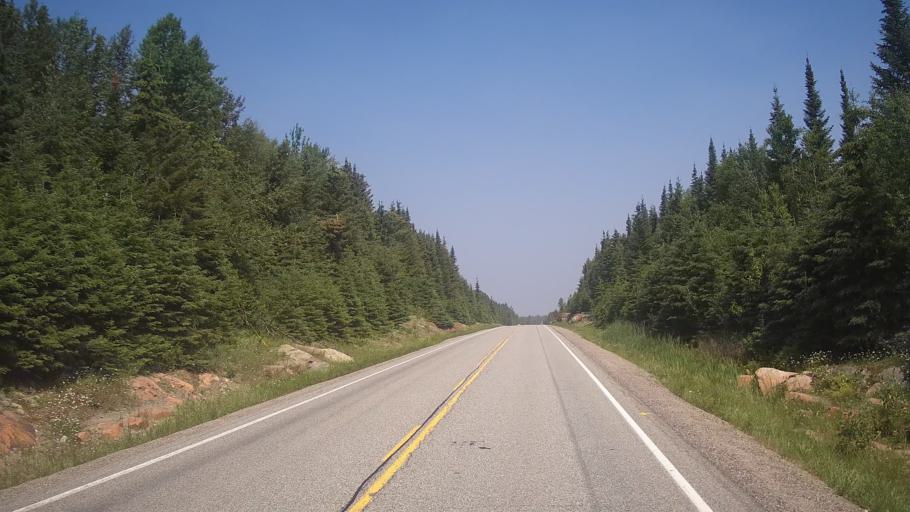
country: CA
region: Ontario
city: Timmins
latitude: 48.1818
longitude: -81.5828
